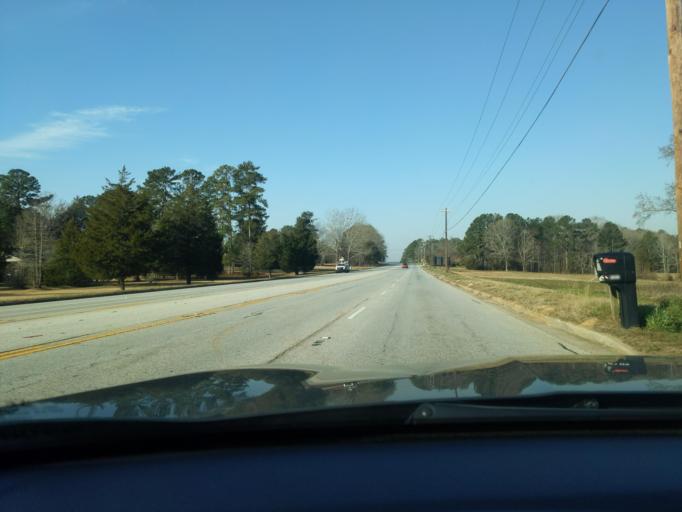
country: US
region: South Carolina
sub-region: Greenwood County
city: Greenwood
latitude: 34.1905
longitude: -82.2340
